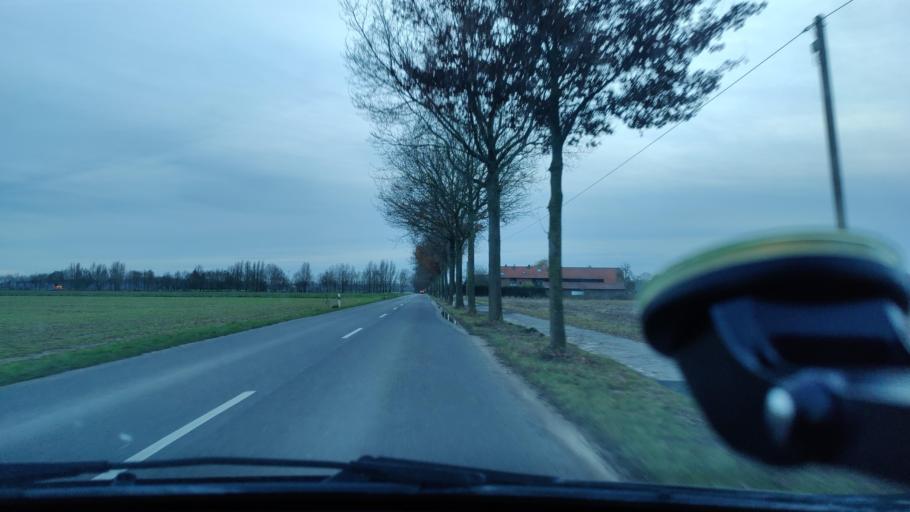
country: DE
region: North Rhine-Westphalia
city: Kalkar
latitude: 51.7577
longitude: 6.3108
